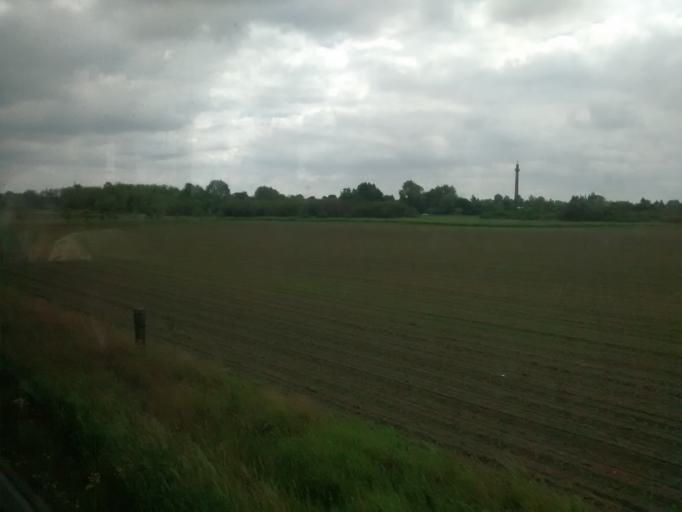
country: DE
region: Berlin
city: Buchholz
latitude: 52.6213
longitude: 13.4401
